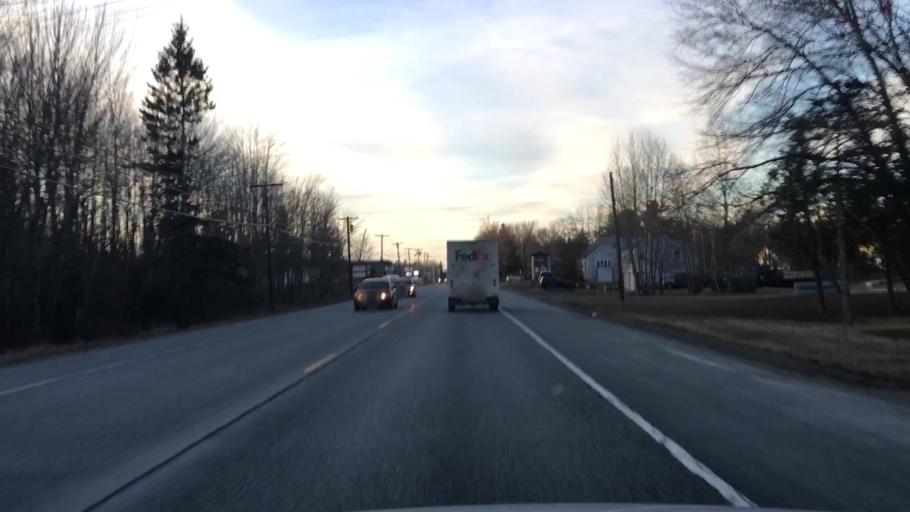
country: US
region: Maine
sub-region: Penobscot County
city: Holden
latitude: 44.7581
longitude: -68.6903
